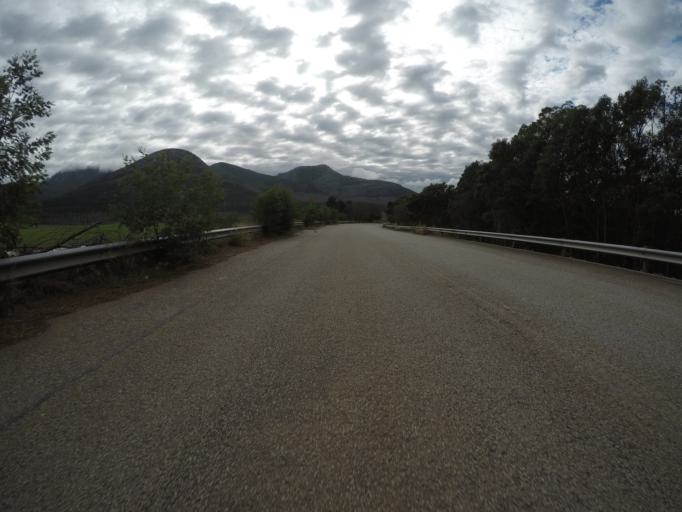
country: ZA
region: Eastern Cape
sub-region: Cacadu District Municipality
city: Kareedouw
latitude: -34.0126
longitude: 24.3085
